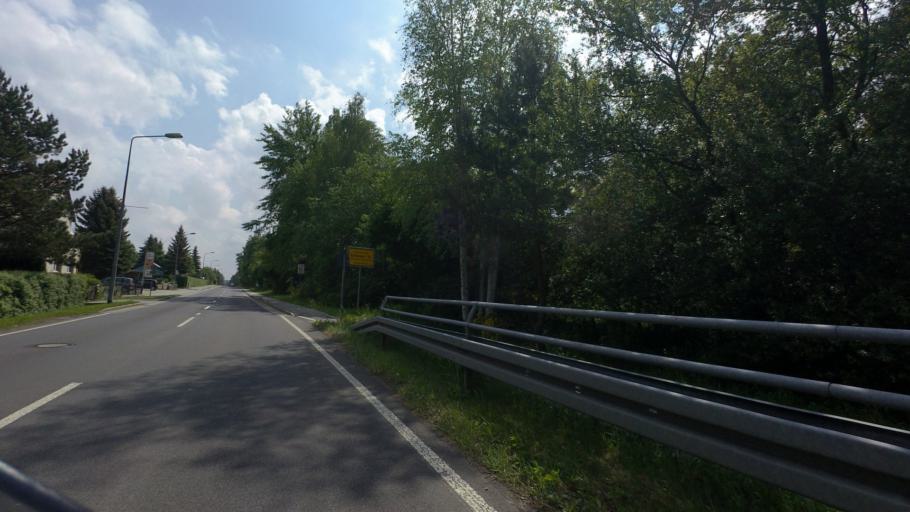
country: DE
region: Saxony
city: Weisswasser
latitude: 51.5187
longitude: 14.6068
